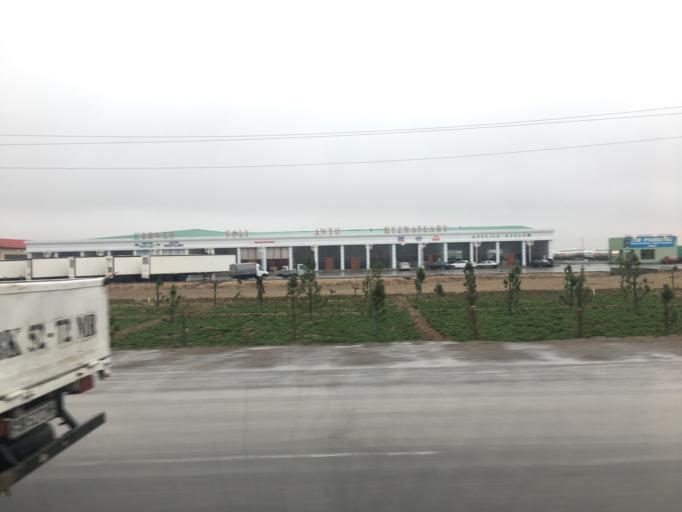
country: TM
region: Mary
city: Mary
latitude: 37.5523
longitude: 61.7502
